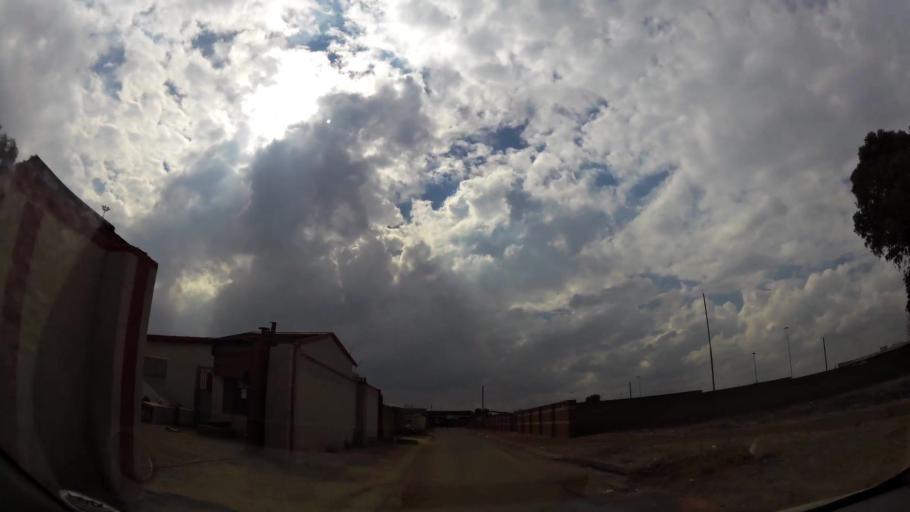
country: ZA
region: Gauteng
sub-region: Ekurhuleni Metropolitan Municipality
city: Germiston
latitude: -26.3880
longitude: 28.1612
